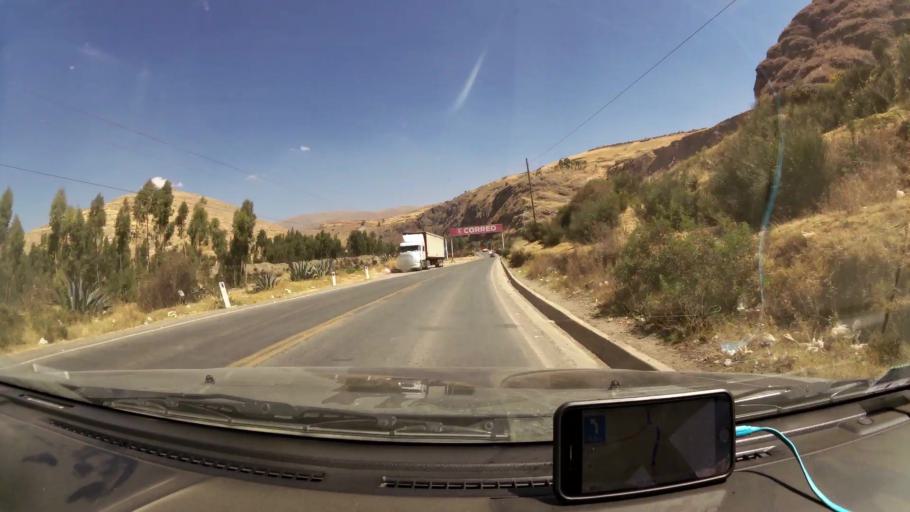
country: PE
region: Junin
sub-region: Provincia de Jauja
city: Sausa
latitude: -11.8017
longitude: -75.4880
